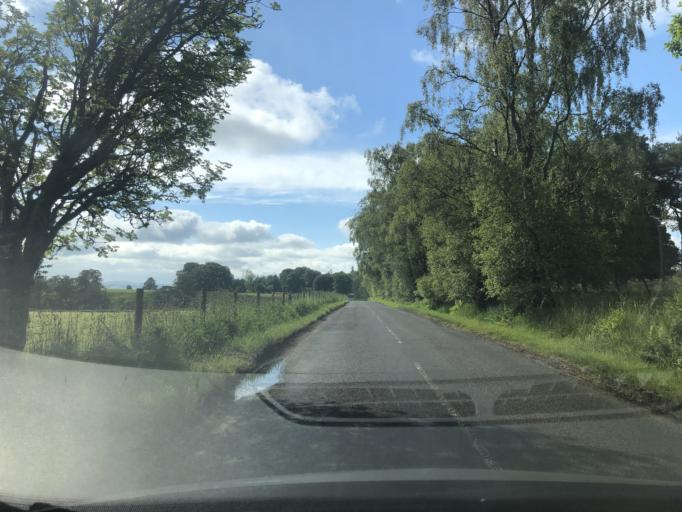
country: GB
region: Scotland
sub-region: Angus
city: Kirriemuir
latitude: 56.7442
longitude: -3.0117
